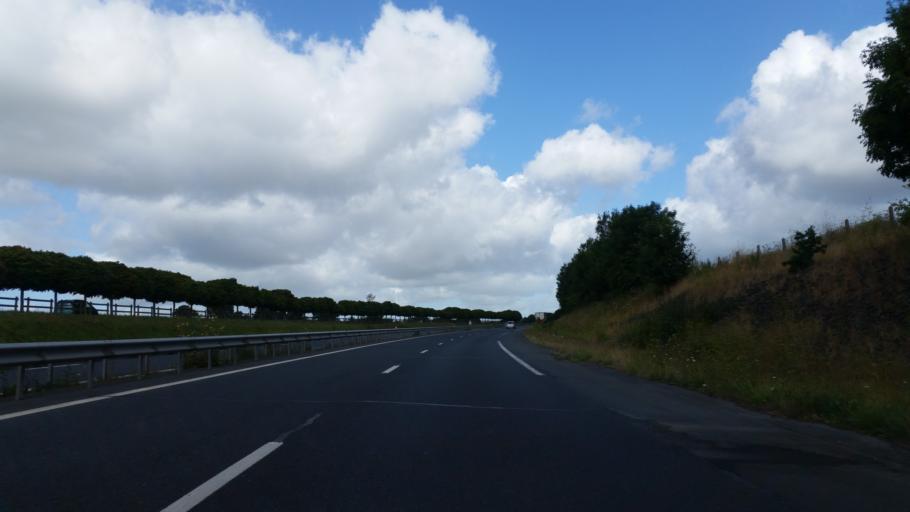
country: FR
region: Lower Normandy
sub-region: Departement du Calvados
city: Grandcamp-Maisy
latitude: 49.3393
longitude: -1.0133
